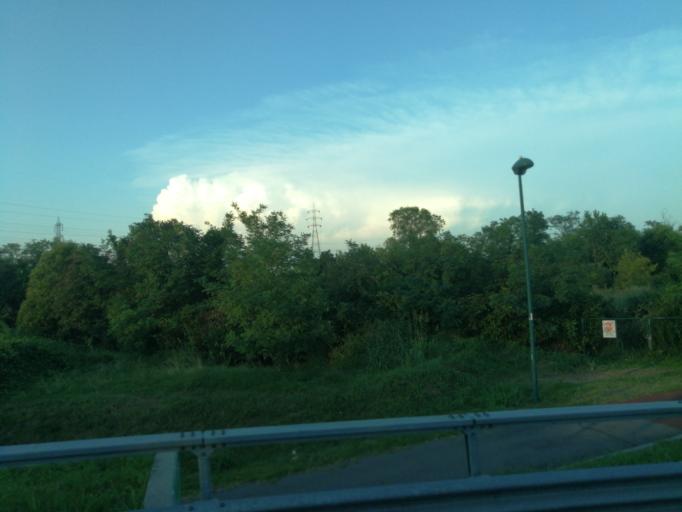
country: IT
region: Lombardy
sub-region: Citta metropolitana di Milano
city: Cologno Monzese
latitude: 45.5355
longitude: 9.2889
